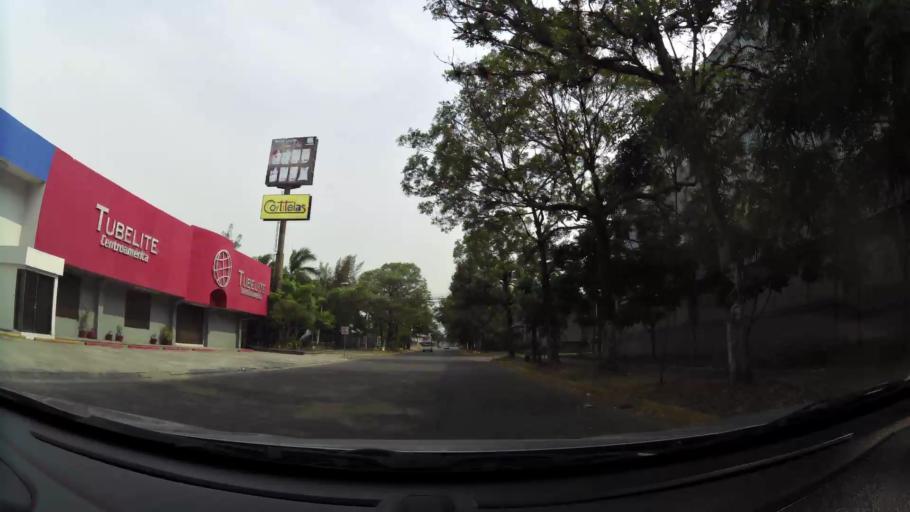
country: HN
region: Cortes
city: San Pedro Sula
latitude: 15.5164
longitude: -88.0238
